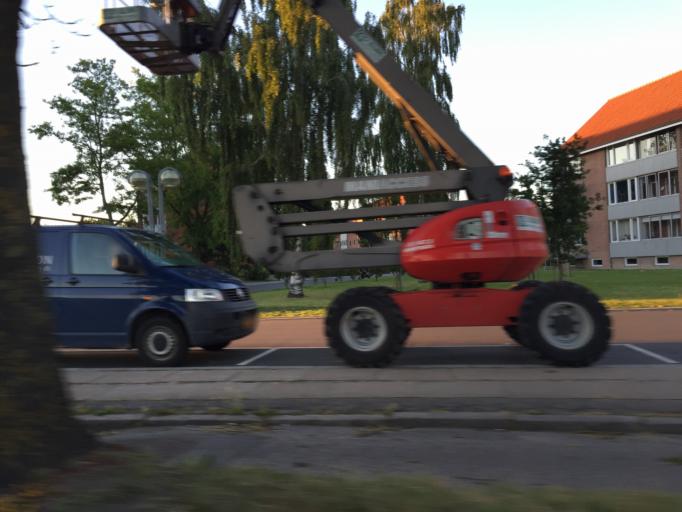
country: DK
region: South Denmark
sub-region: Nyborg Kommune
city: Nyborg
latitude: 55.3192
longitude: 10.7802
